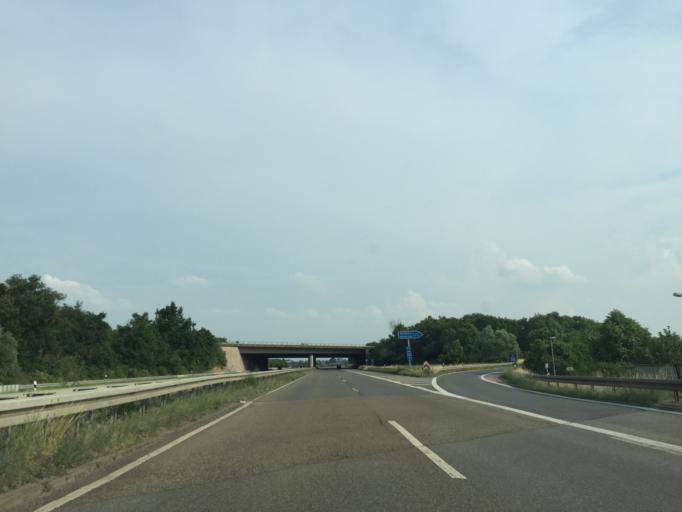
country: DE
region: Baden-Wuerttemberg
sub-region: Karlsruhe Region
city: Bruhl
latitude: 49.4100
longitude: 8.5454
